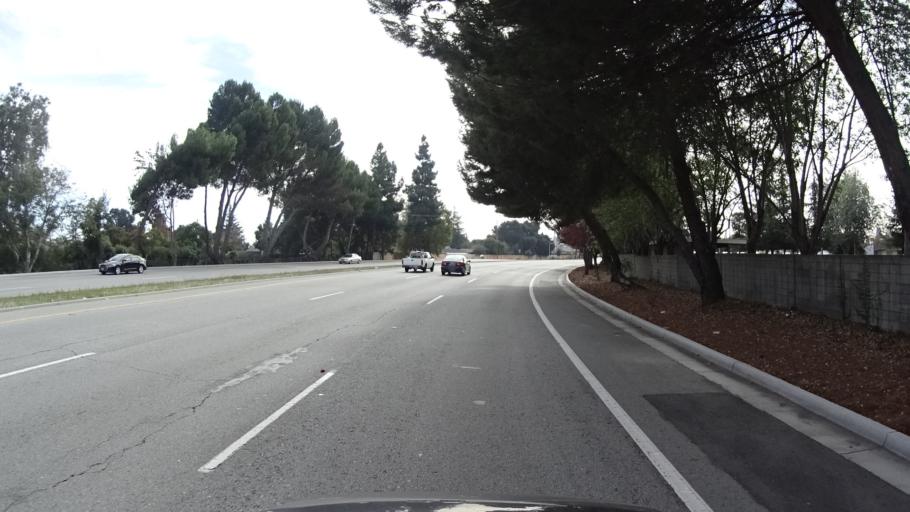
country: US
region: California
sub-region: Santa Clara County
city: Santa Clara
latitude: 37.3261
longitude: -121.9649
